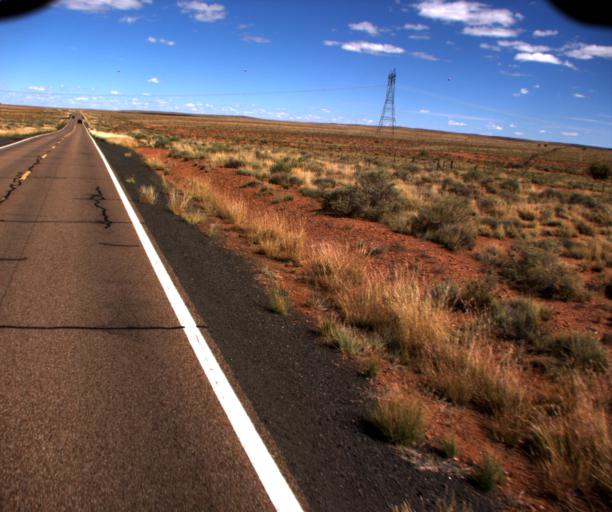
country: US
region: Arizona
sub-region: Navajo County
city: Holbrook
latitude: 34.7912
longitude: -110.2196
